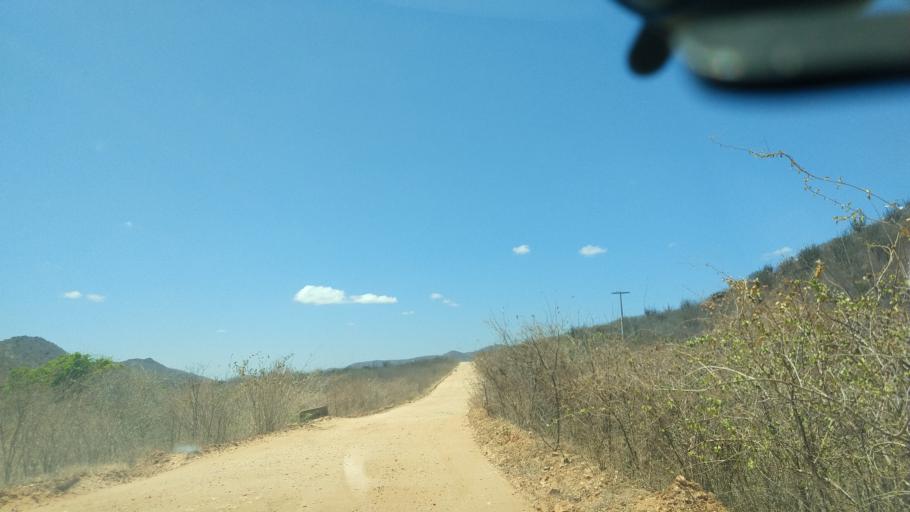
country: BR
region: Rio Grande do Norte
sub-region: Sao Tome
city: Sao Tome
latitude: -5.9703
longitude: -36.1620
